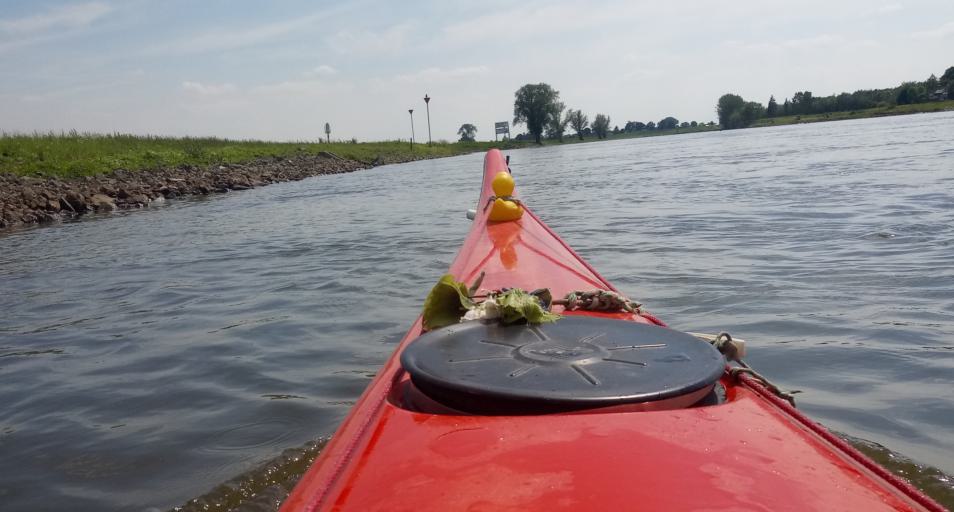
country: NL
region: Gelderland
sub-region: Gemeente Zutphen
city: Zutphen
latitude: 52.1617
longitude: 6.1861
